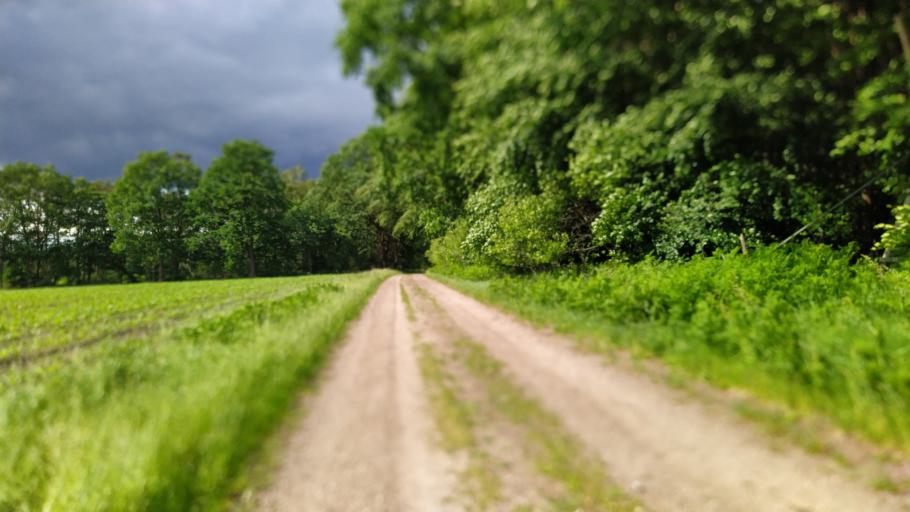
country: DE
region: Lower Saxony
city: Deinstedt
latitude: 53.4392
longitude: 9.2598
